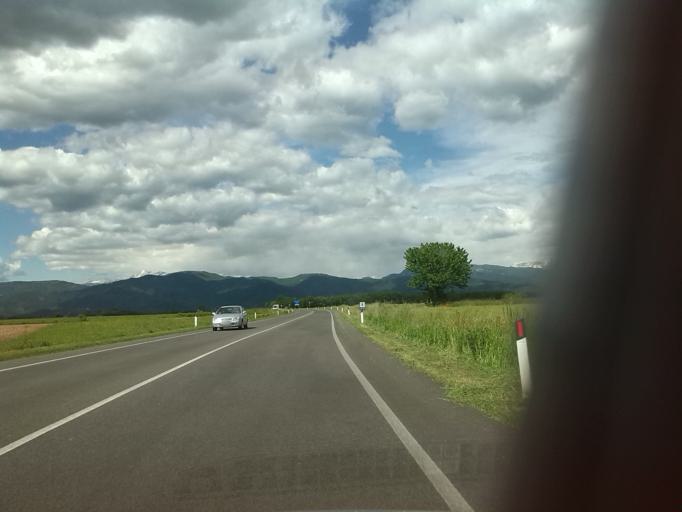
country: IT
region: Friuli Venezia Giulia
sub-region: Provincia di Udine
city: Orsaria
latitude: 46.0453
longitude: 13.3765
